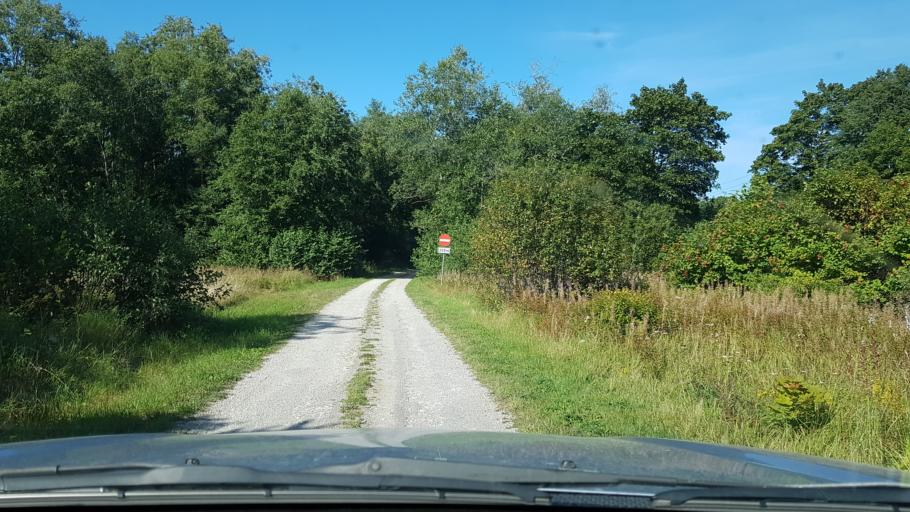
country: EE
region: Ida-Virumaa
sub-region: Sillamaee linn
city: Sillamae
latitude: 59.3936
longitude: 27.8778
